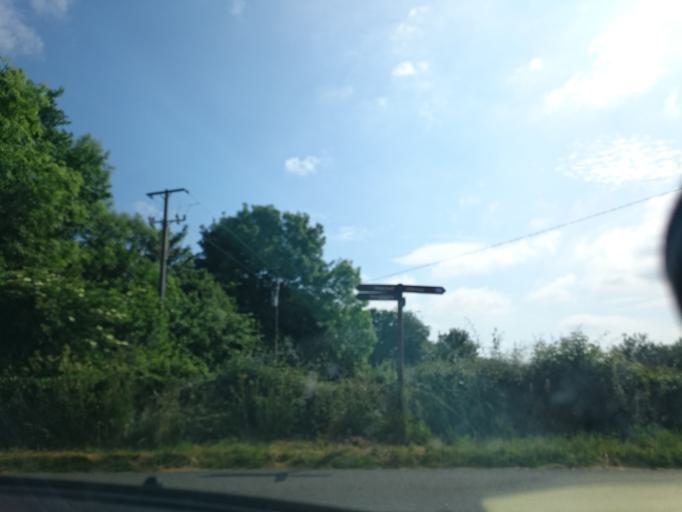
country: IE
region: Leinster
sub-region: Kilkenny
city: Thomastown
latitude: 52.5201
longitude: -7.1907
